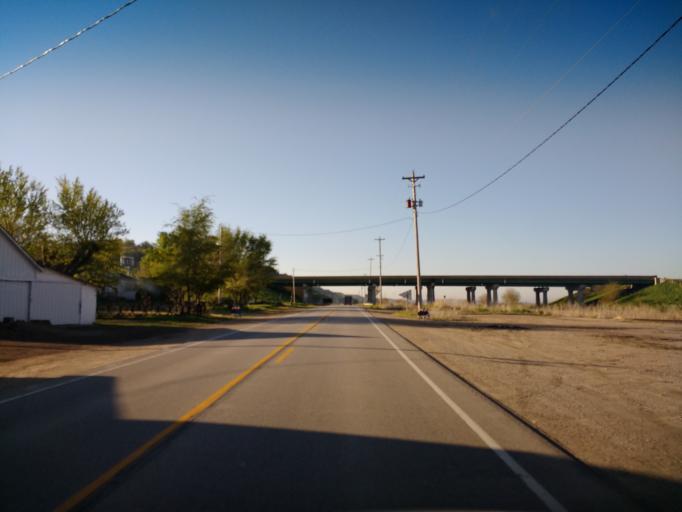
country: US
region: Iowa
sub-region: Harrison County
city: Missouri Valley
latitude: 41.4964
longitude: -95.8921
